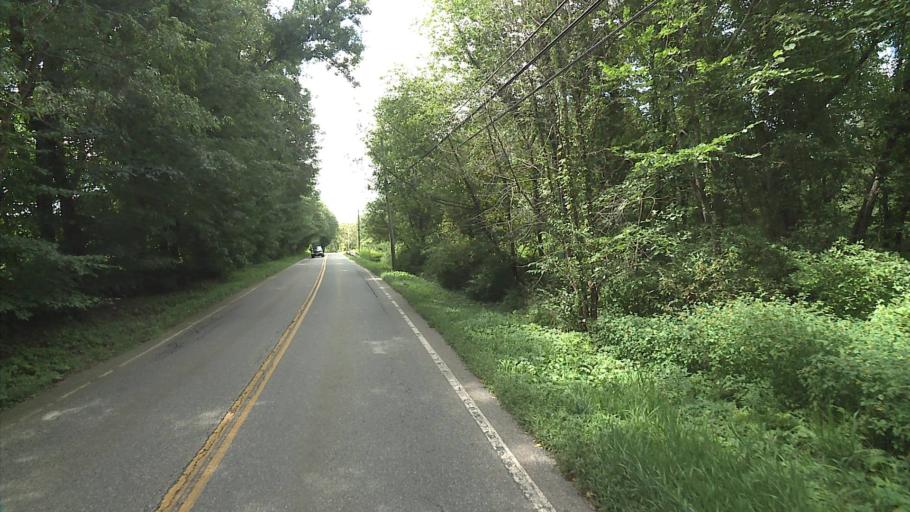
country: US
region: Connecticut
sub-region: Windham County
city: South Windham
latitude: 41.6467
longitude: -72.1975
